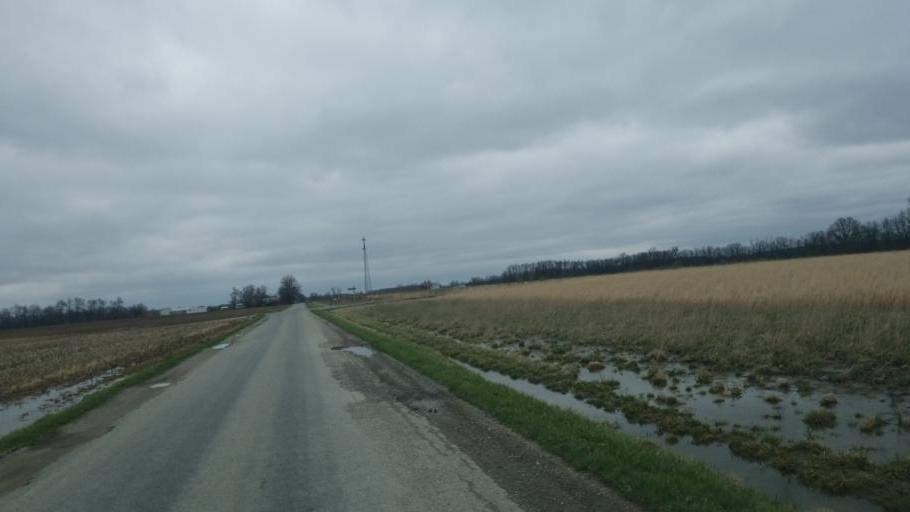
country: US
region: Ohio
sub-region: Wyandot County
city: Upper Sandusky
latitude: 40.6860
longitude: -83.3812
